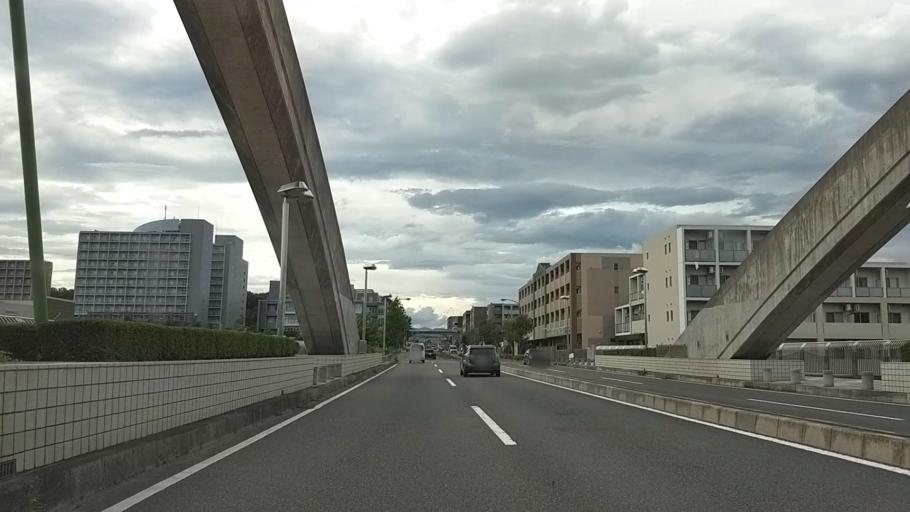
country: JP
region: Tokyo
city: Hachioji
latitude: 35.6328
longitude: 139.3323
